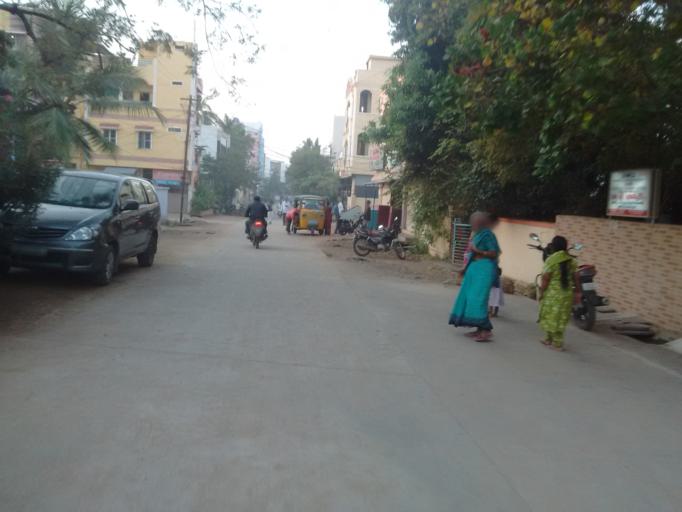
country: IN
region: Telangana
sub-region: Mahbubnagar
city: Alampur
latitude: 15.8101
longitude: 78.0418
